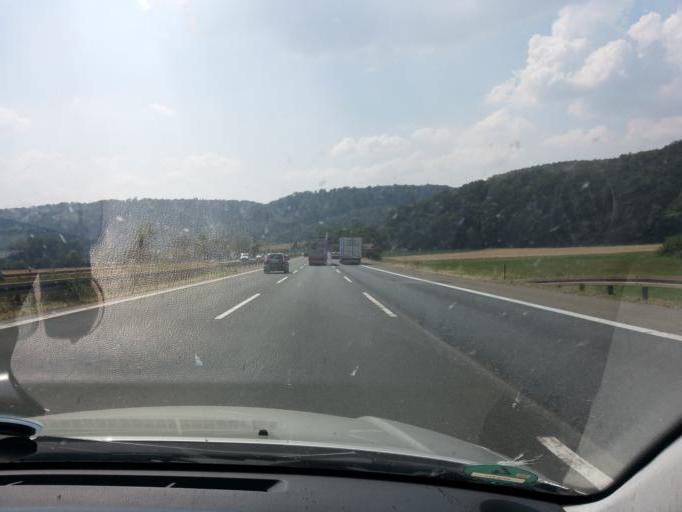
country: DE
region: Bavaria
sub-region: Regierungsbezirk Mittelfranken
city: Greding
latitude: 49.0164
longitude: 11.3599
